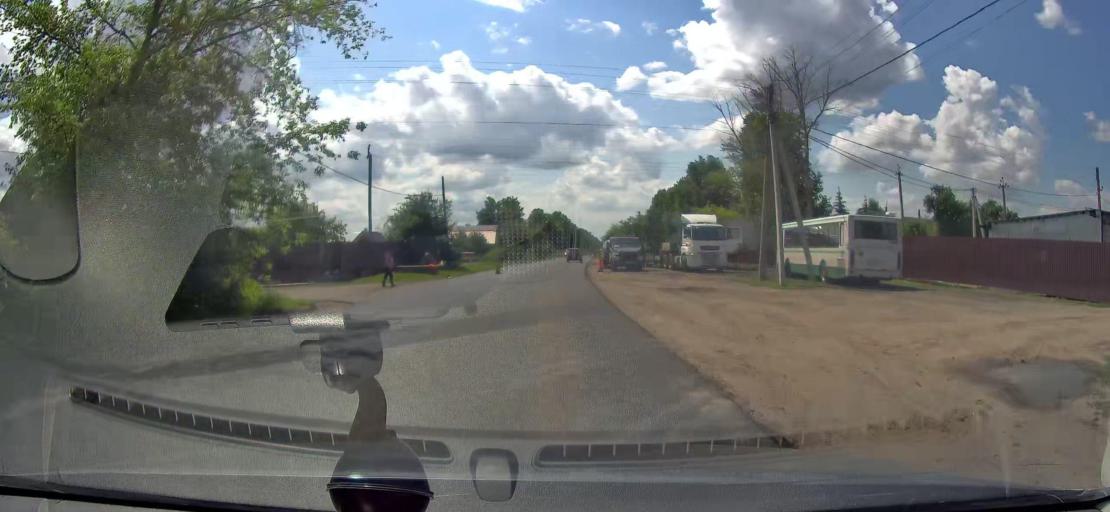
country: RU
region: Kursk
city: Zolotukhino
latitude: 51.9722
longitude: 36.2957
